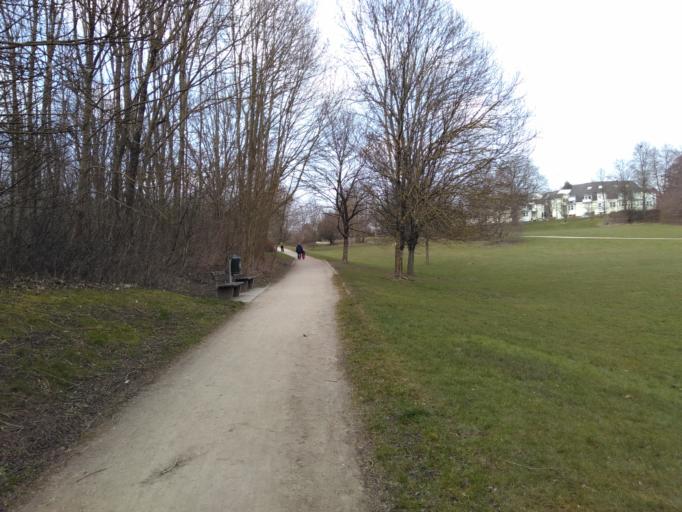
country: DE
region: North Rhine-Westphalia
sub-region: Regierungsbezirk Koln
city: Aachen
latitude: 50.7771
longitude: 6.0524
